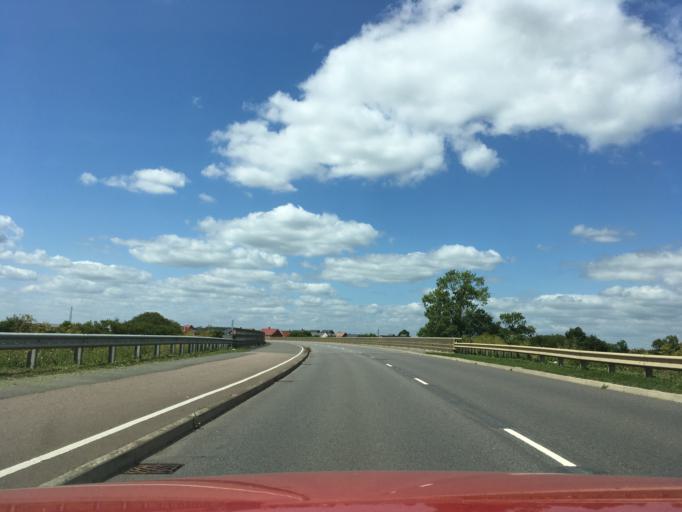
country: GB
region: England
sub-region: Buckinghamshire
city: Aylesbury
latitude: 51.8392
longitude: -0.8424
